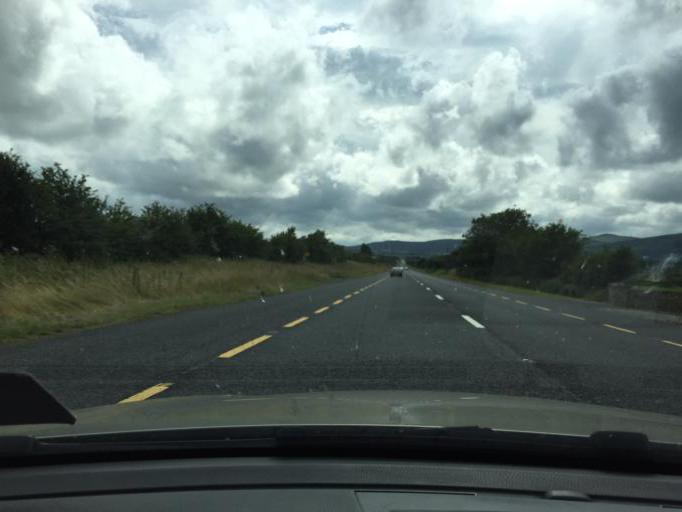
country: IE
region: Munster
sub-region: Waterford
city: Dungarvan
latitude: 52.1791
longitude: -7.4966
